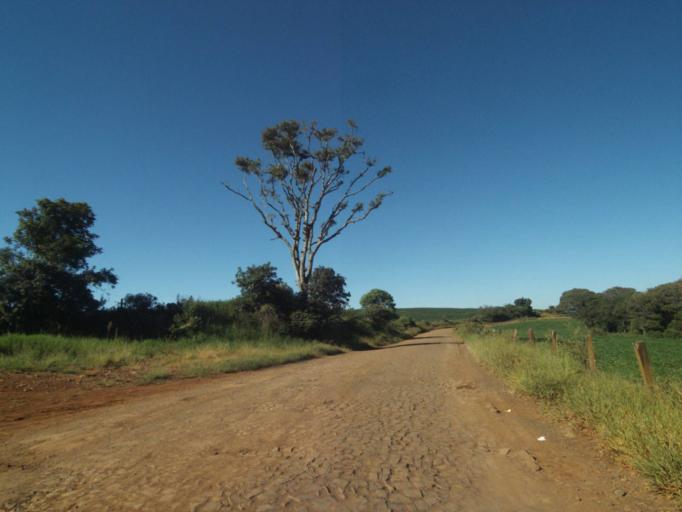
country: BR
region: Parana
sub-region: Pinhao
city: Pinhao
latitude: -25.8456
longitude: -52.0320
